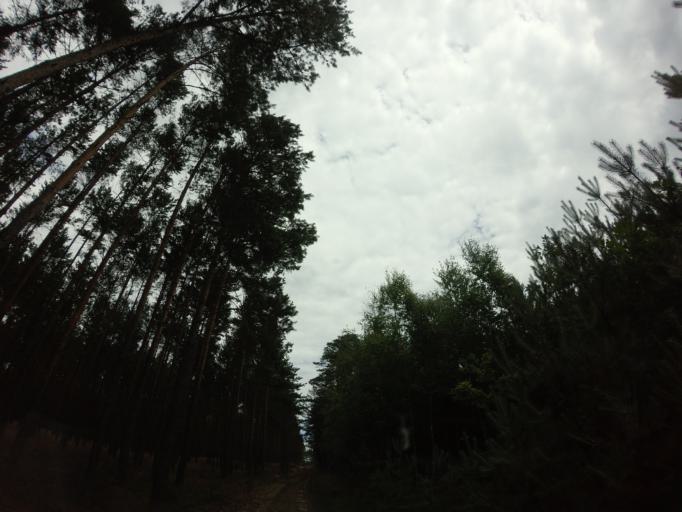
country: PL
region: West Pomeranian Voivodeship
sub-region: Powiat choszczenski
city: Drawno
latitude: 53.1479
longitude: 15.7736
